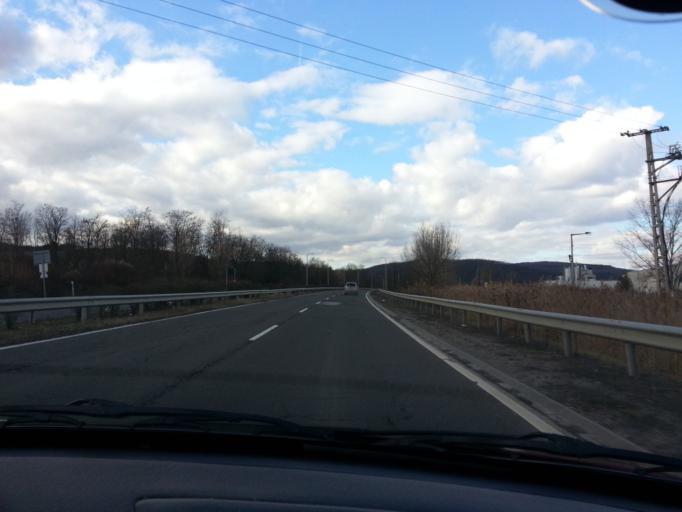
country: HU
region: Nograd
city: Salgotarjan
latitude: 48.0455
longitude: 19.7879
